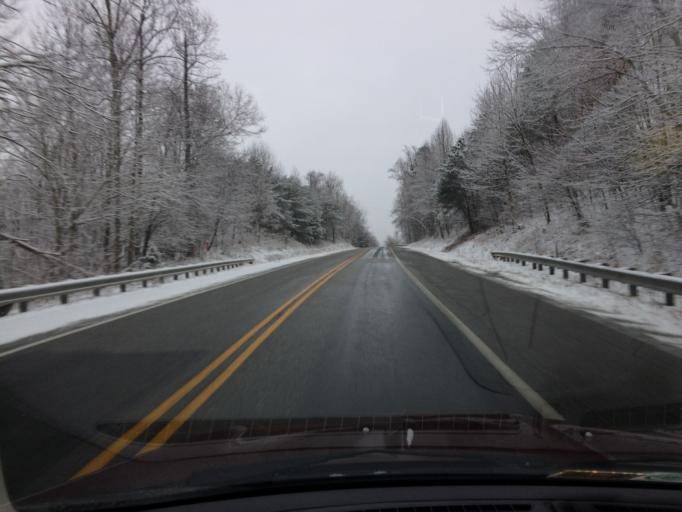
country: US
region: Virginia
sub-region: Amherst County
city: Amherst
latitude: 37.6569
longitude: -79.1409
